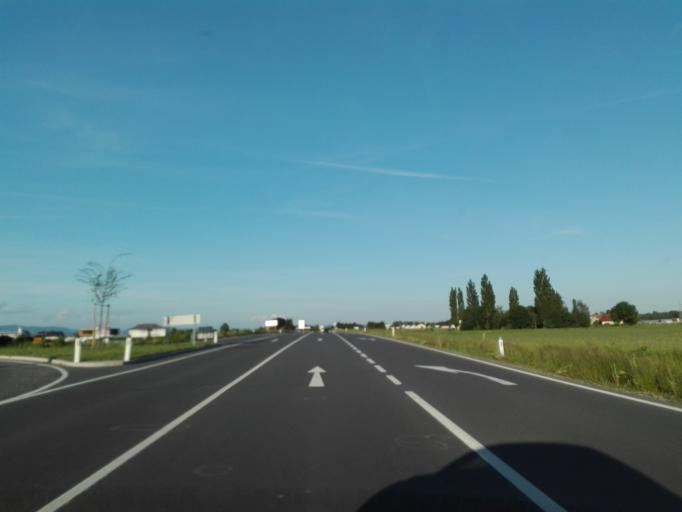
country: AT
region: Upper Austria
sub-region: Politischer Bezirk Urfahr-Umgebung
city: Feldkirchen an der Donau
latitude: 48.2981
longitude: 14.0145
